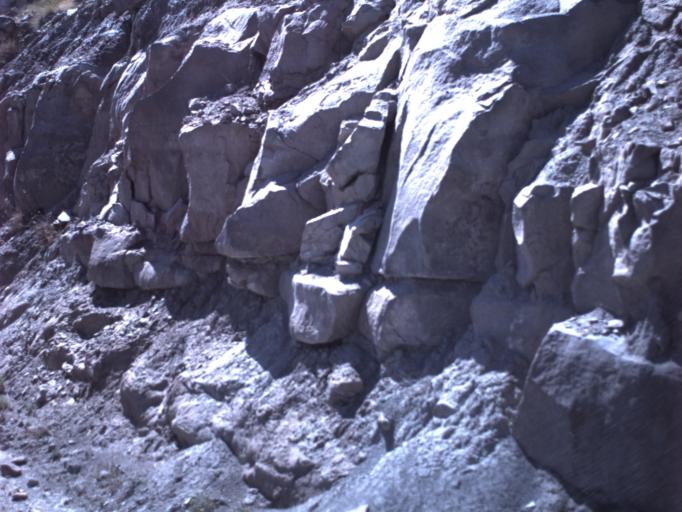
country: US
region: Utah
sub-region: Grand County
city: Moab
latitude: 38.8249
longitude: -109.2841
